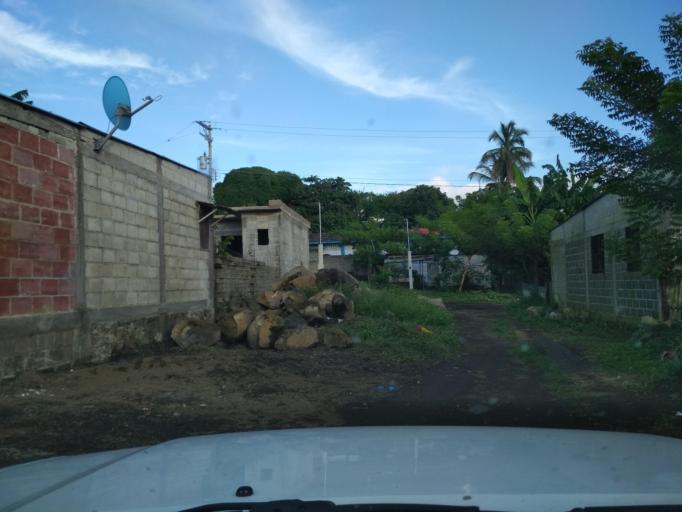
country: MX
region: Veracruz
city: Catemaco
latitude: 18.4207
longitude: -95.1229
